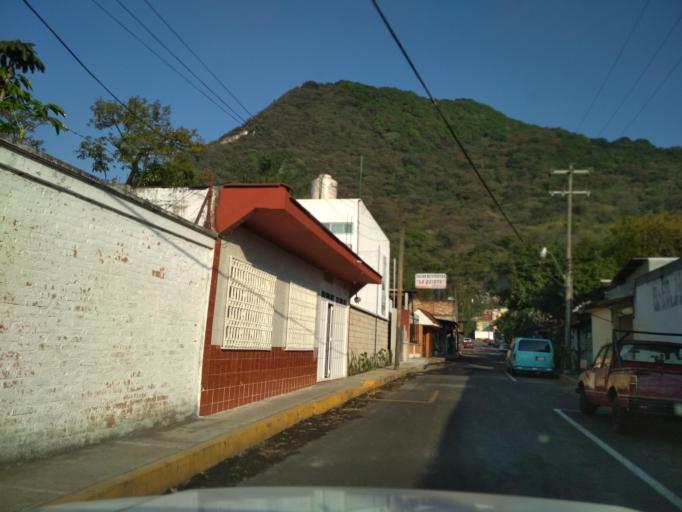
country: MX
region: Veracruz
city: Ixtac Zoquitlan
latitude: 18.8587
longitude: -97.0798
